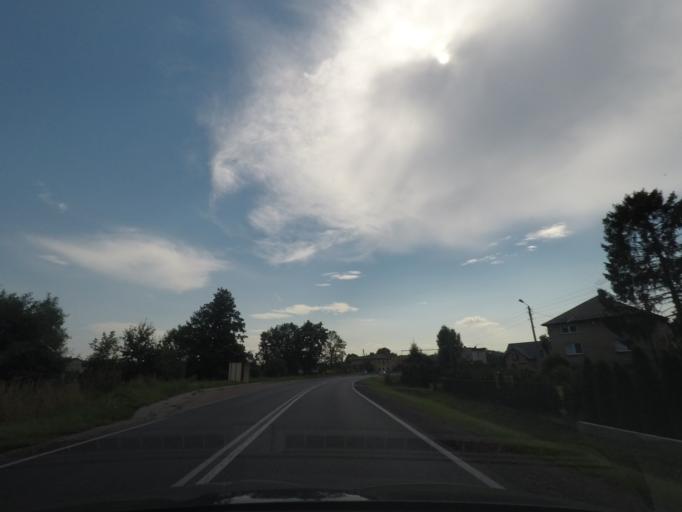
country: PL
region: Lesser Poland Voivodeship
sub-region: Powiat oswiecimski
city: Rajsko
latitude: 50.0053
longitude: 19.1835
